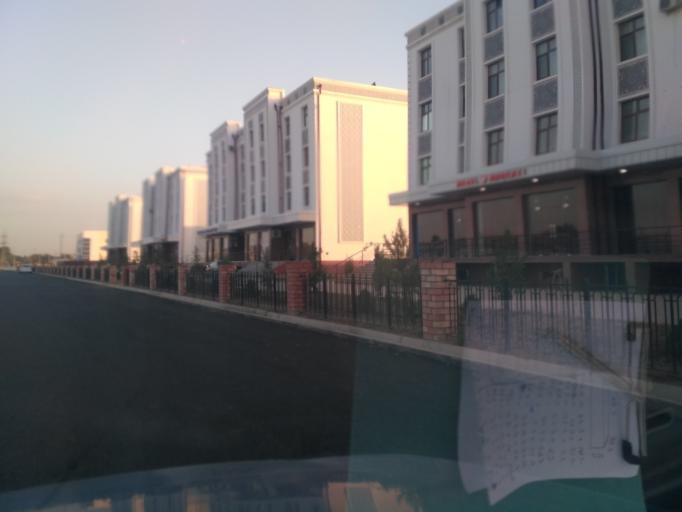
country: UZ
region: Sirdaryo
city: Guliston
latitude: 40.5074
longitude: 68.7672
